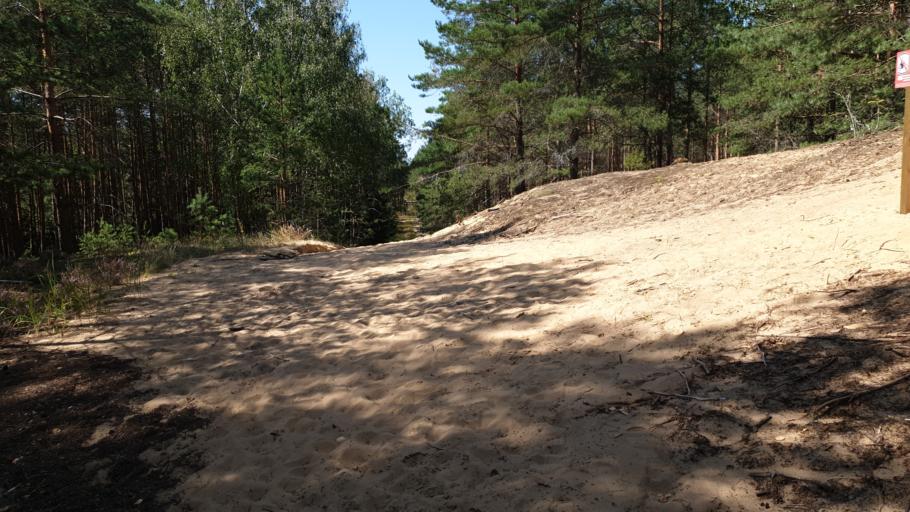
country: LT
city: Sirvintos
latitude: 54.8917
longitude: 24.9533
